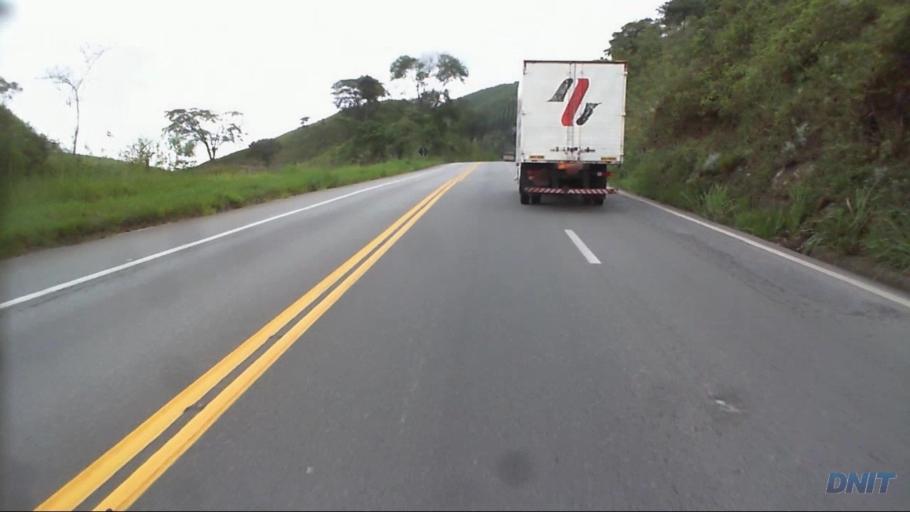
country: BR
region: Minas Gerais
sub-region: Nova Era
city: Nova Era
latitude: -19.6668
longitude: -42.9654
